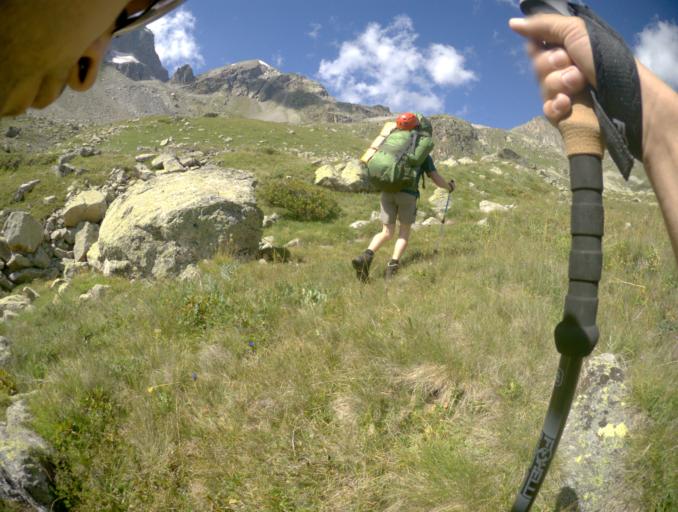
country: RU
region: Karachayevo-Cherkesiya
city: Uchkulan
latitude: 43.3252
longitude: 42.1027
